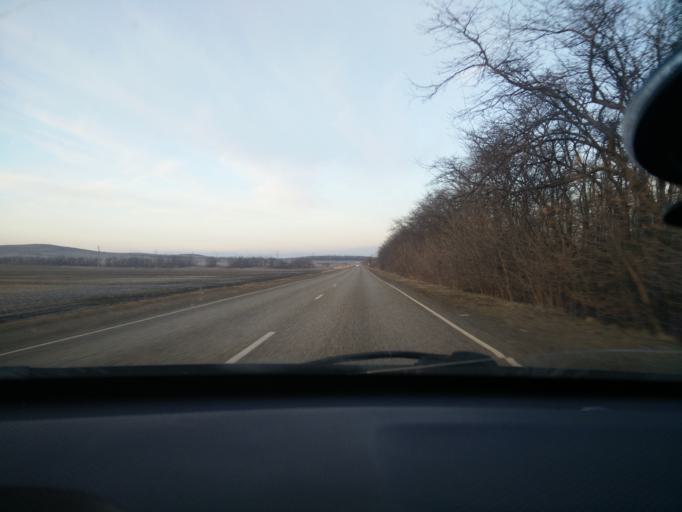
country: RU
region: Stavropol'skiy
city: Tatarka
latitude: 44.9951
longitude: 41.7303
